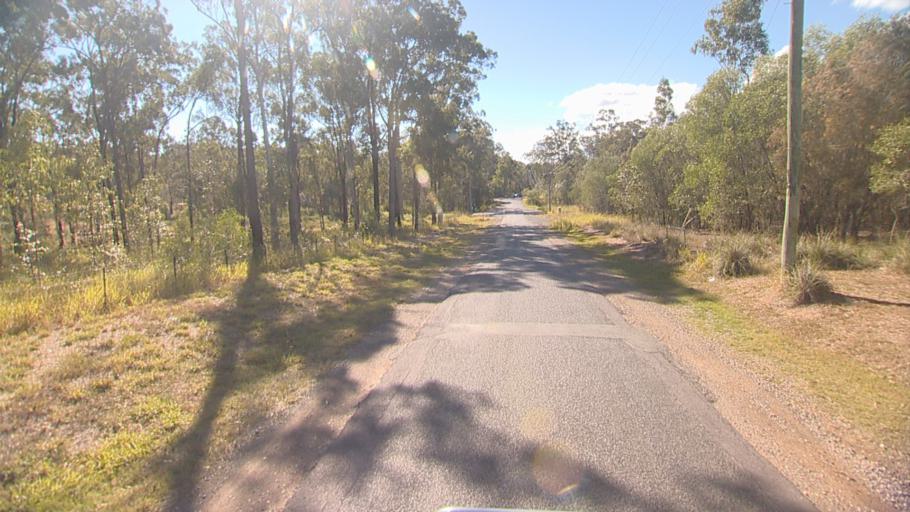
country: AU
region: Queensland
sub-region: Logan
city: Chambers Flat
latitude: -27.8050
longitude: 153.0828
